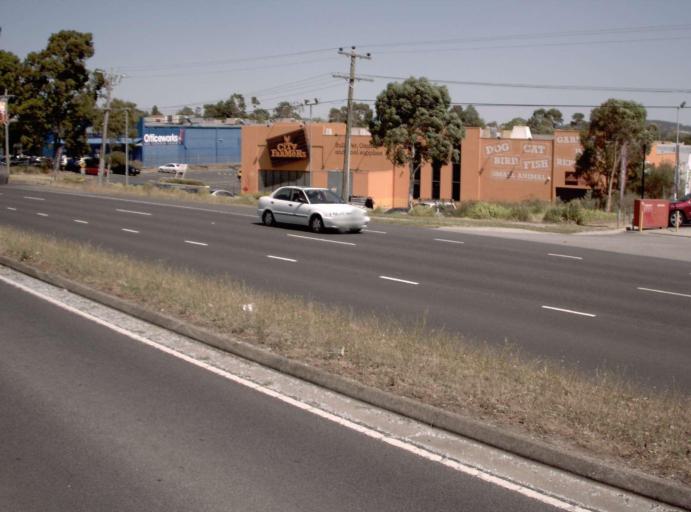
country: AU
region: Victoria
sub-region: Knox
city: Boronia
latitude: -37.8809
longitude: 145.2721
